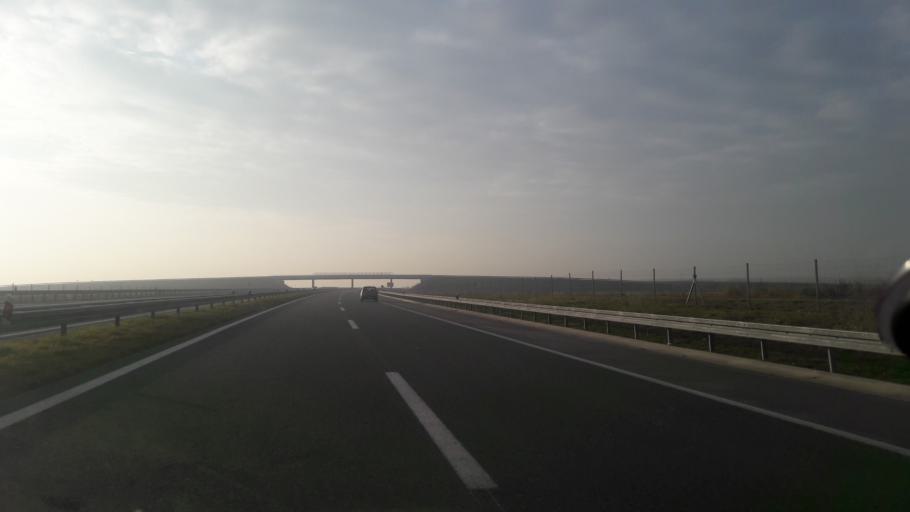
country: HR
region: Osjecko-Baranjska
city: Gorjani
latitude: 45.3537
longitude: 18.4008
